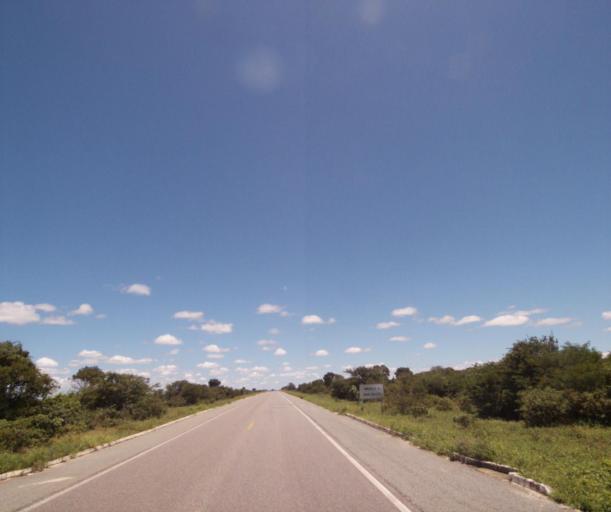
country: BR
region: Bahia
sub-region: Carinhanha
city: Carinhanha
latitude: -14.3051
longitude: -43.7852
